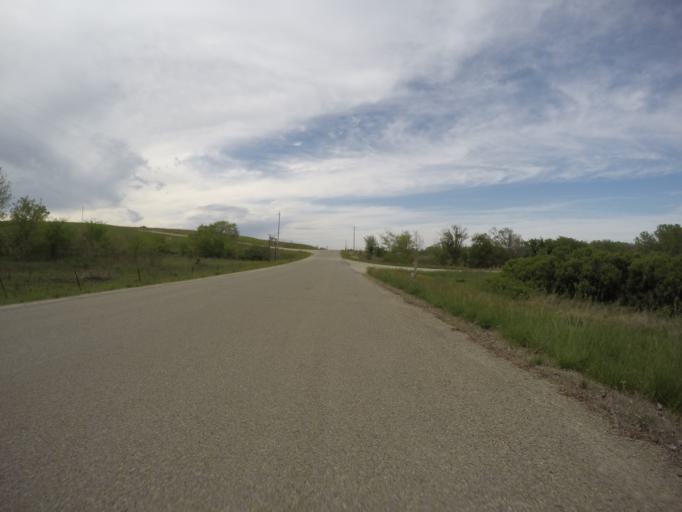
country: US
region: Kansas
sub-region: Riley County
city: Ogden
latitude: 39.0062
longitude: -96.6023
